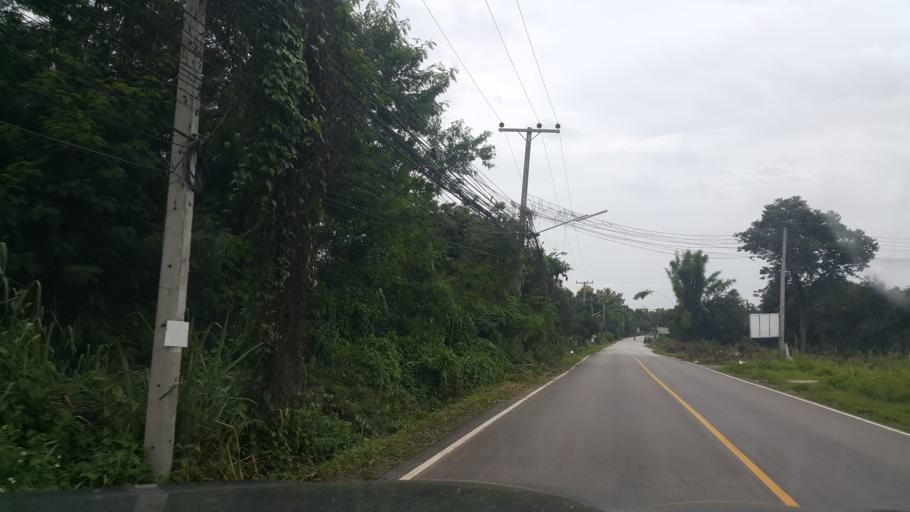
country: TH
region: Chiang Mai
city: San Sai
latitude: 18.9116
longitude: 99.0173
